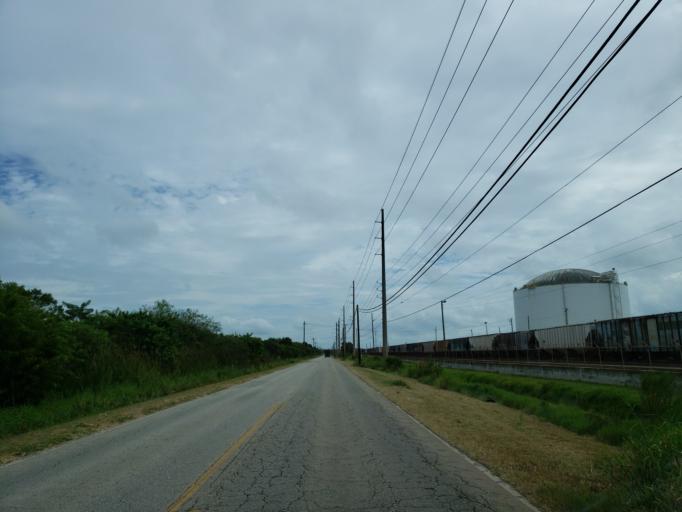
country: US
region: Florida
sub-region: Hillsborough County
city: Palm River-Clair Mel
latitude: 27.9063
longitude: -82.4134
